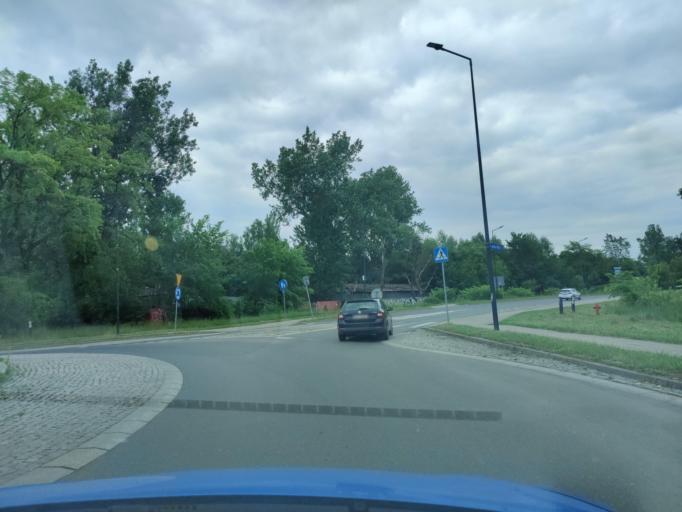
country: PL
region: Silesian Voivodeship
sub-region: Myslowice
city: Myslowice
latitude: 50.2549
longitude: 19.1508
